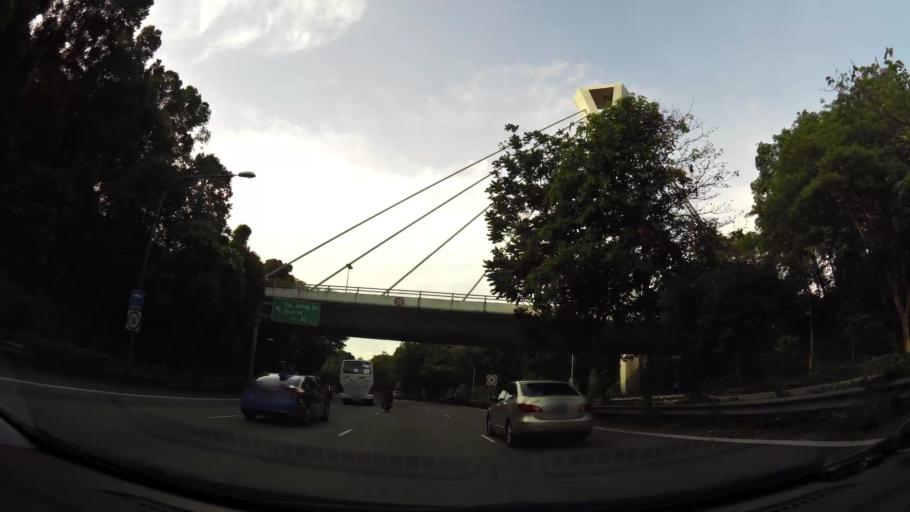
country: MY
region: Johor
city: Johor Bahru
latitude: 1.3385
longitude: 103.6777
